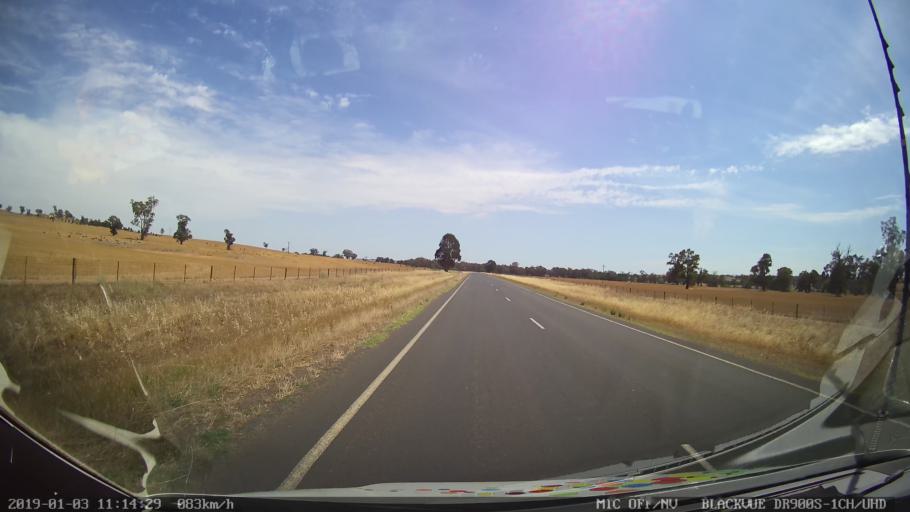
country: AU
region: New South Wales
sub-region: Young
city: Young
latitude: -34.1755
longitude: 148.2609
